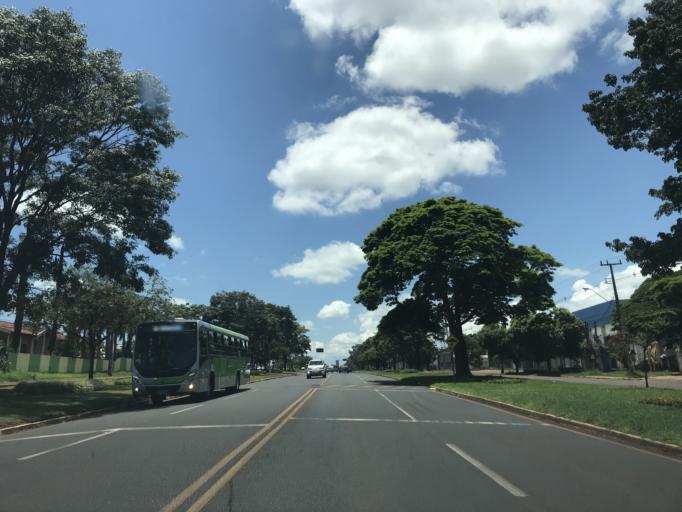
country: BR
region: Parana
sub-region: Marialva
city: Marialva
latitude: -23.4737
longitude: -51.8156
